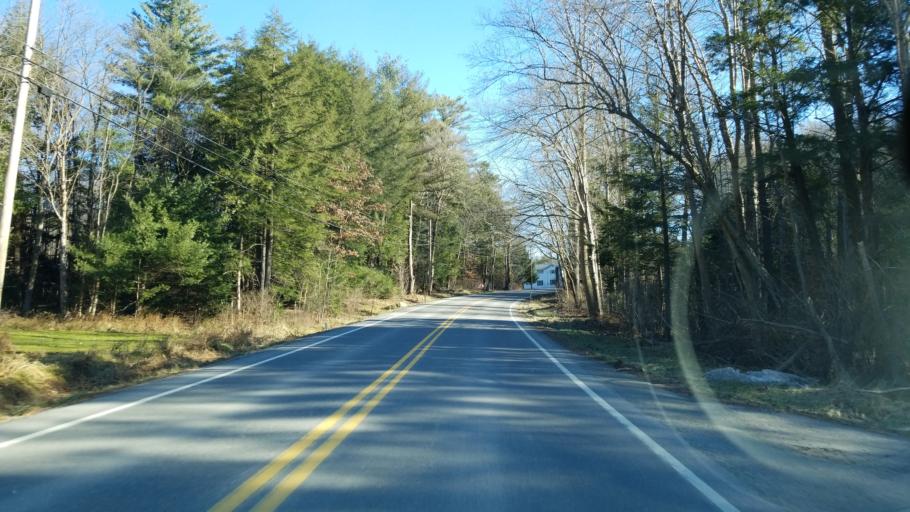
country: US
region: Pennsylvania
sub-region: Jefferson County
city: Falls Creek
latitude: 41.1767
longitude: -78.8409
